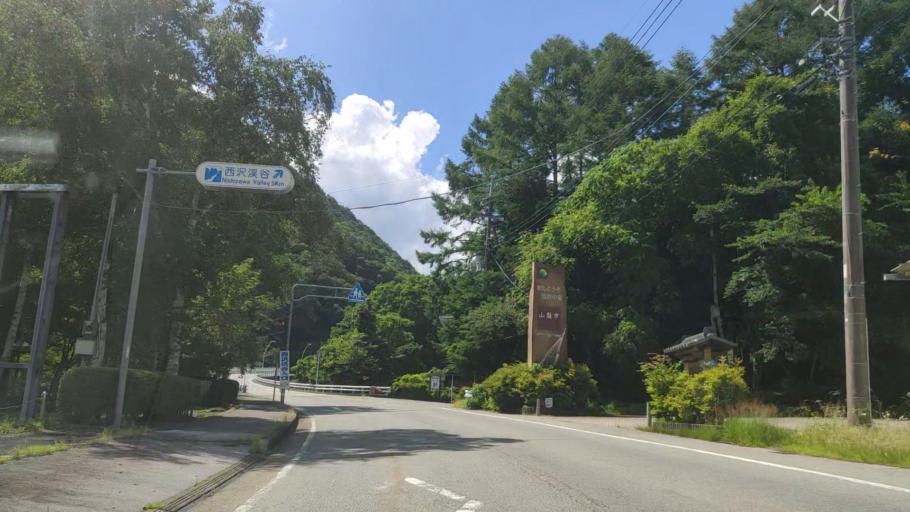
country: JP
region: Yamanashi
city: Enzan
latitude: 35.8617
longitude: 138.7561
